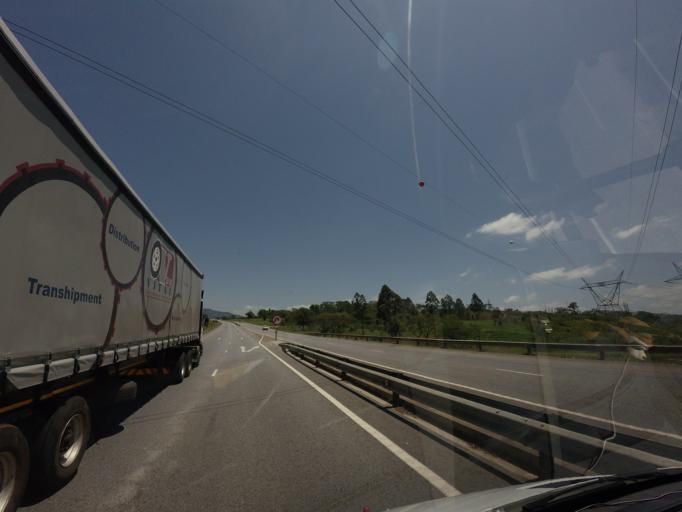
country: ZA
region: Mpumalanga
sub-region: Ehlanzeni District
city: Nelspruit
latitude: -25.4430
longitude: 30.8125
